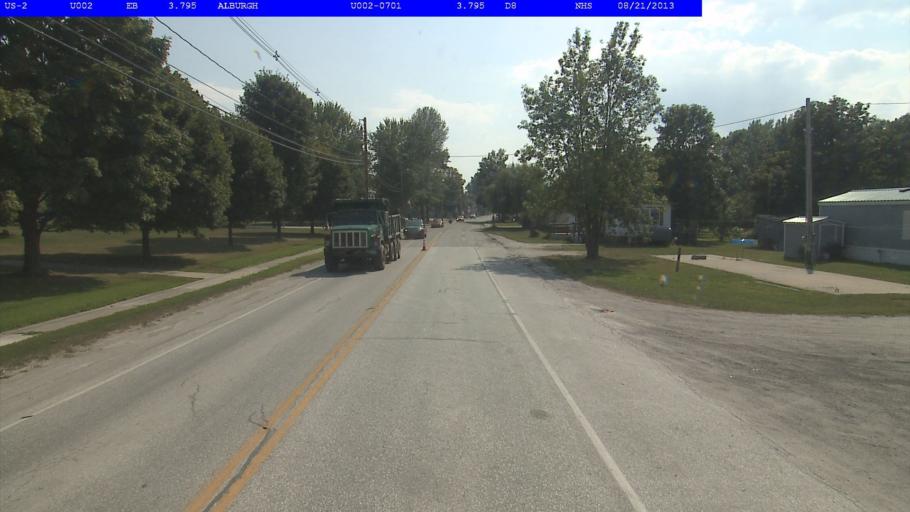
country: US
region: New York
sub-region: Clinton County
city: Rouses Point
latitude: 44.9793
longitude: -73.2987
